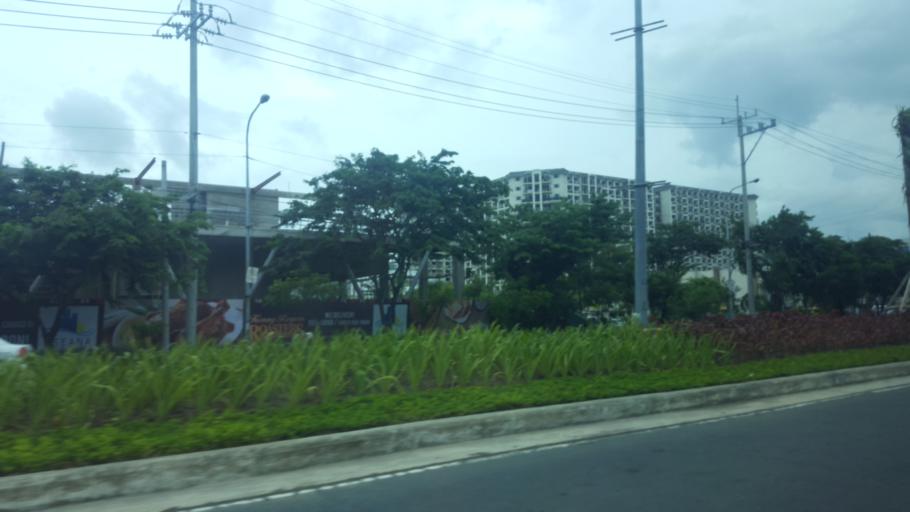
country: PH
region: Metro Manila
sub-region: Makati City
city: Makati City
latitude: 14.5283
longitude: 120.9900
